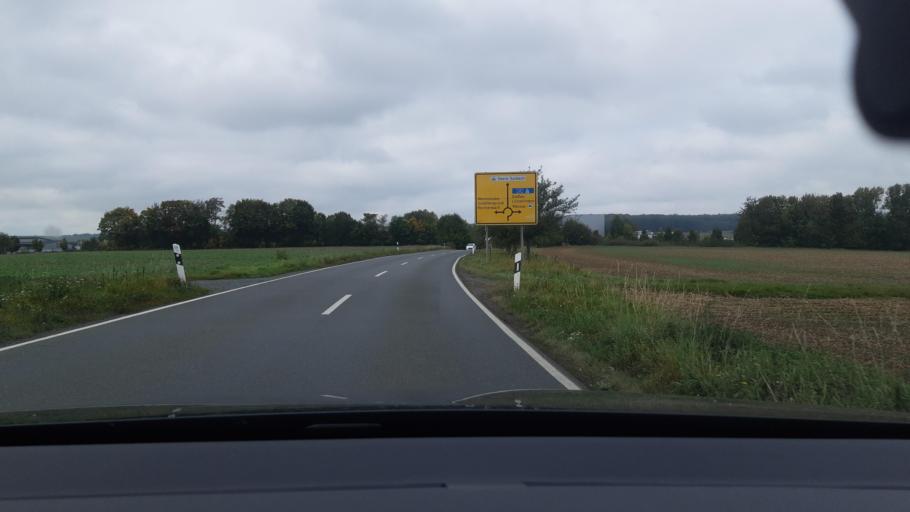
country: DE
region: Hesse
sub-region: Regierungsbezirk Giessen
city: Hoernsheim
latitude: 50.5229
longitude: 8.5973
